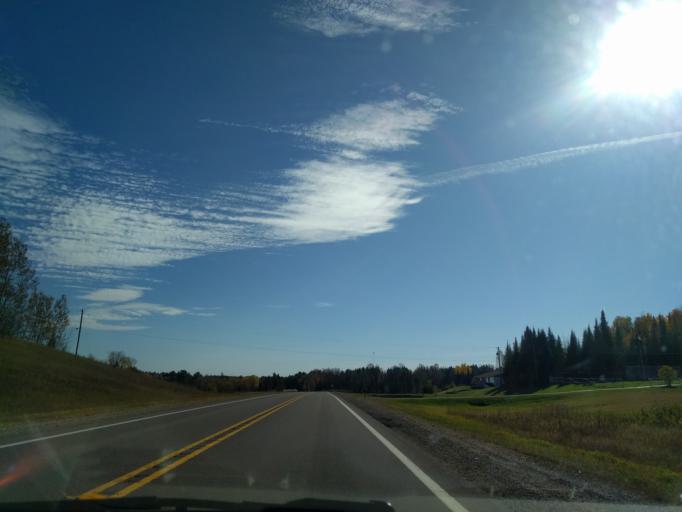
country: US
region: Michigan
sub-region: Marquette County
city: West Ishpeming
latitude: 46.3559
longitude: -87.9830
